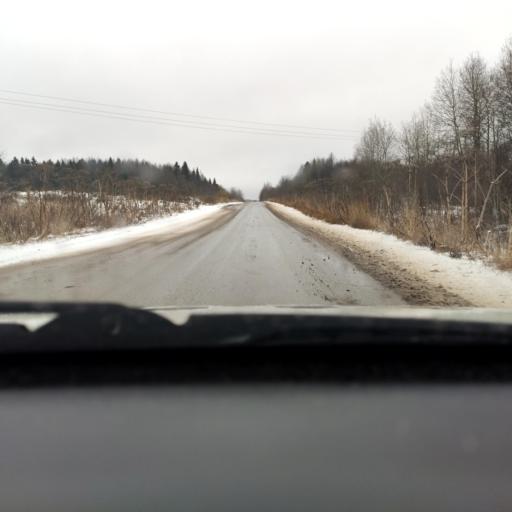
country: RU
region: Perm
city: Ferma
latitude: 57.9896
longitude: 56.3730
